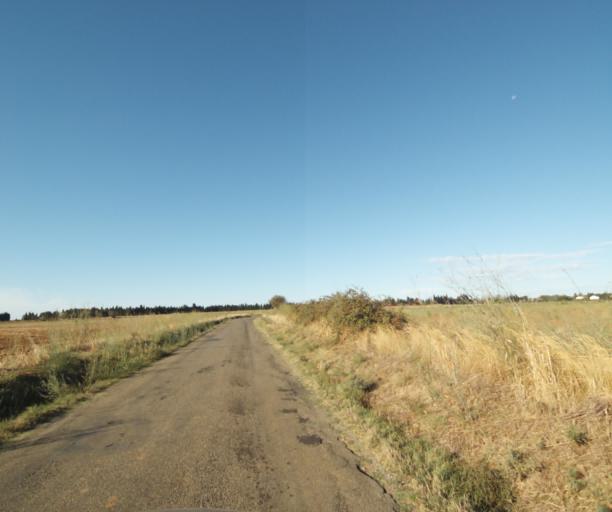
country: FR
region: Languedoc-Roussillon
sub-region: Departement du Gard
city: Bouillargues
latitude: 43.7988
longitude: 4.4457
